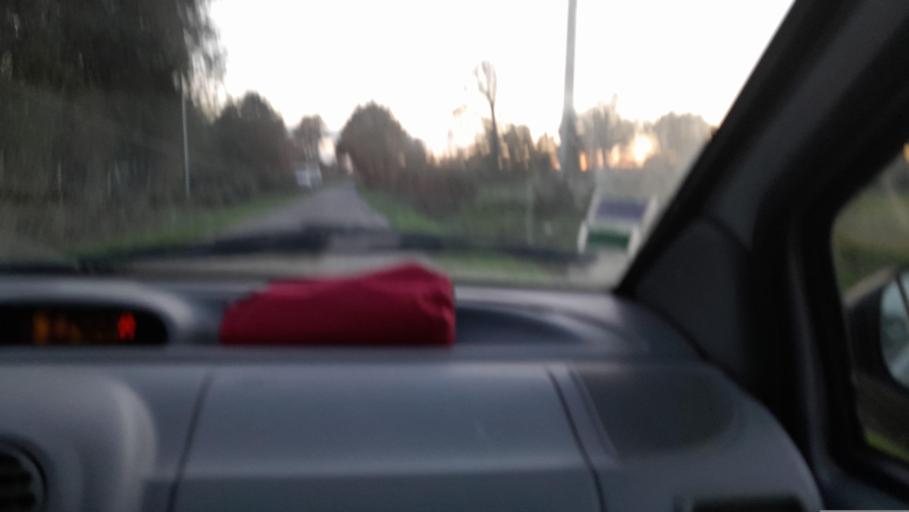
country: FR
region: Brittany
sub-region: Departement d'Ille-et-Vilaine
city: Rannee
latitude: 47.8764
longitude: -1.1836
